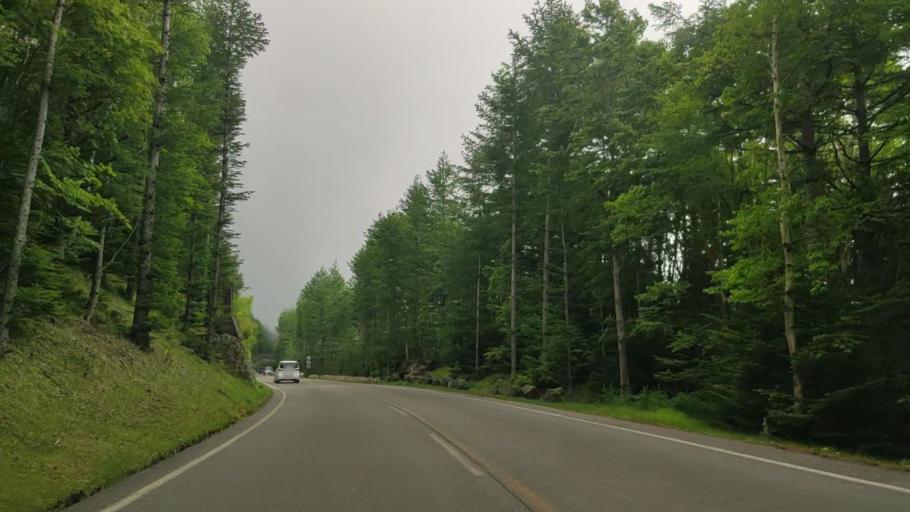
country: JP
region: Yamanashi
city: Fujikawaguchiko
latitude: 35.3788
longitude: 138.6908
